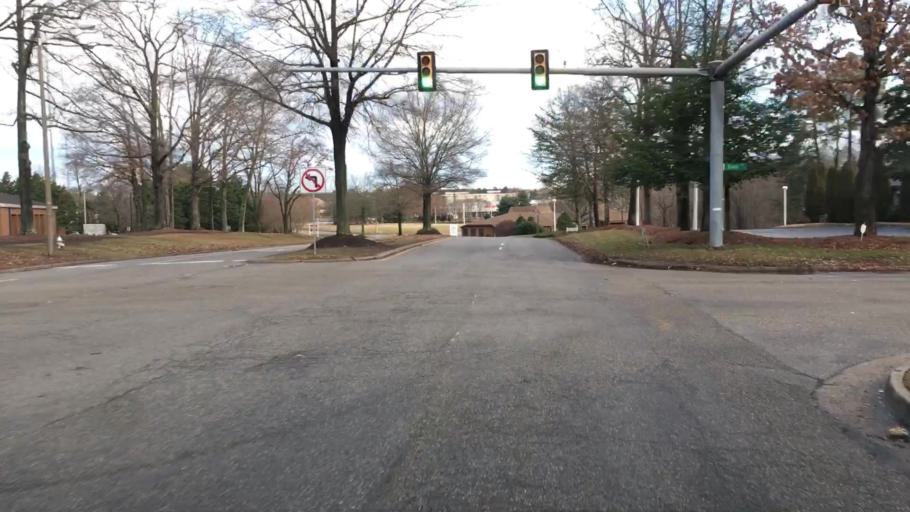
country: US
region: Virginia
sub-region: Chesterfield County
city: Bon Air
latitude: 37.5001
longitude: -77.5970
